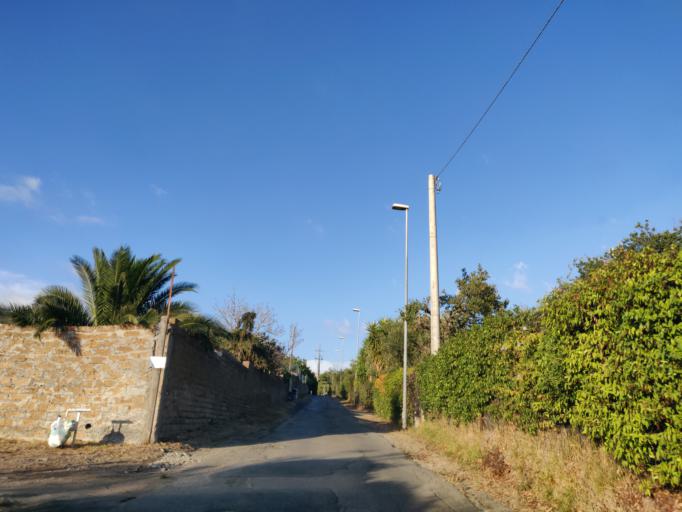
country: IT
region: Latium
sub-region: Citta metropolitana di Roma Capitale
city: Civitavecchia
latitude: 42.0913
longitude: 11.8151
